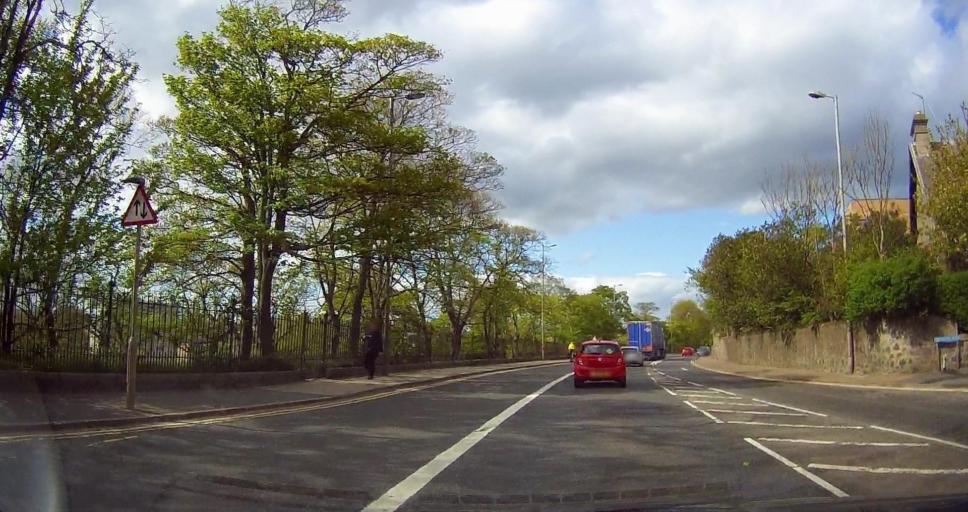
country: GB
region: Scotland
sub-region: Aberdeen City
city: Aberdeen
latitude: 57.1315
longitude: -2.0945
